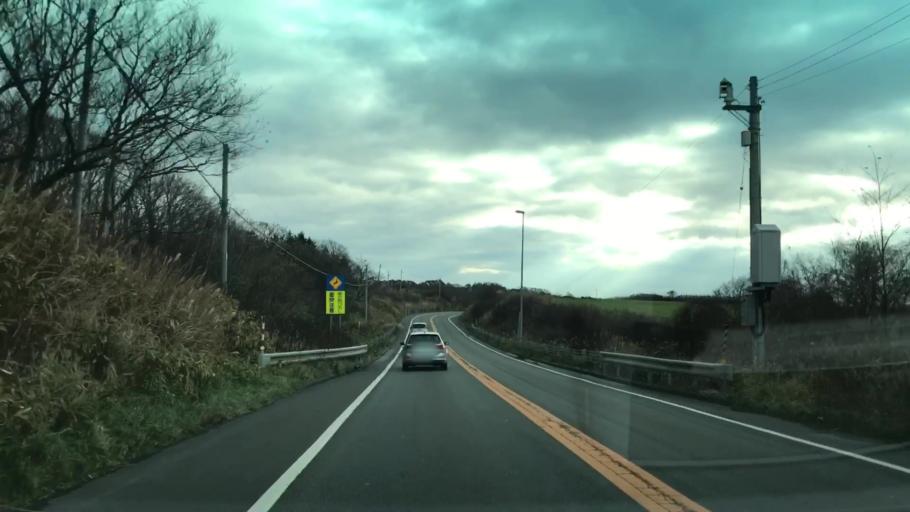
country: JP
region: Hokkaido
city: Shizunai-furukawacho
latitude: 42.4138
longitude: 142.2388
